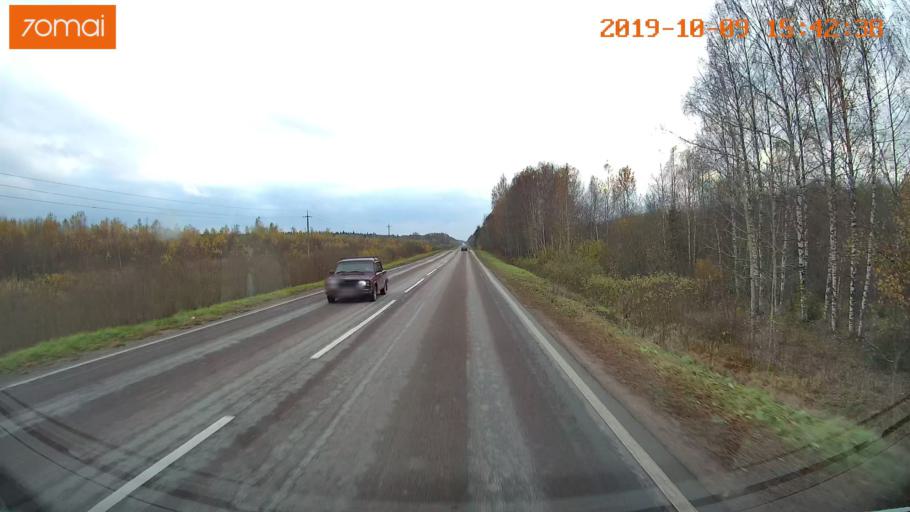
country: RU
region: Kostroma
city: Oktyabr'skiy
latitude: 57.8662
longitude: 41.1032
